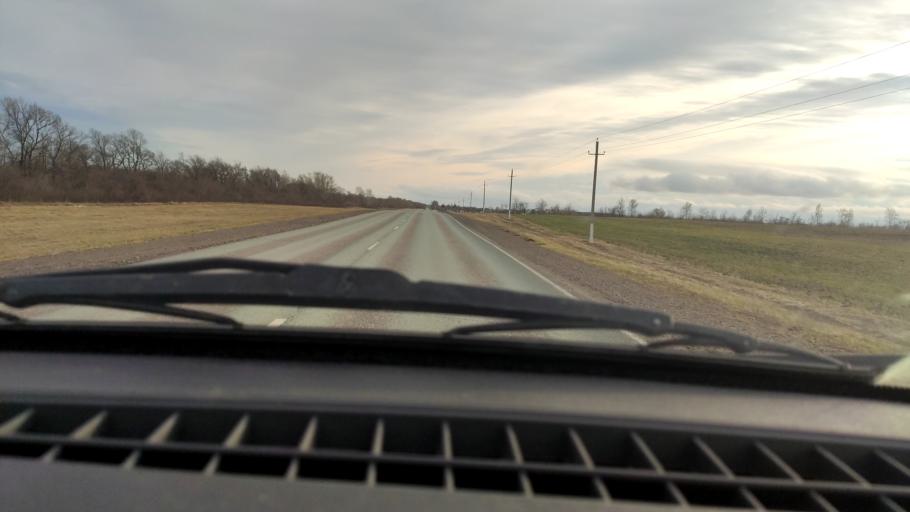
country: RU
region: Bashkortostan
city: Davlekanovo
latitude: 54.3075
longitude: 55.1401
